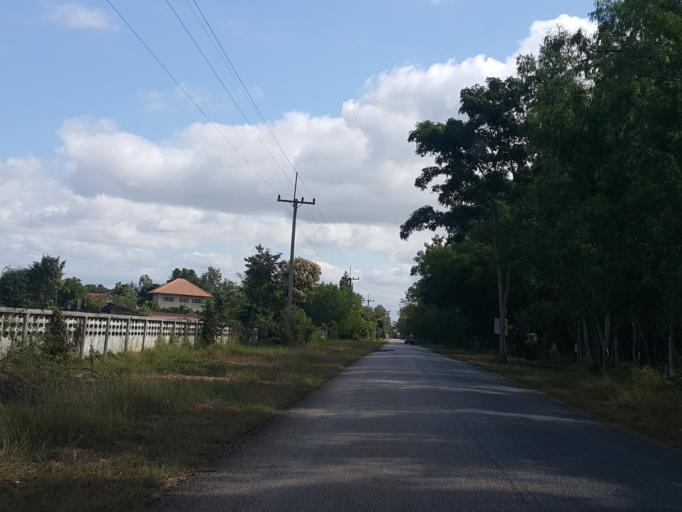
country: TH
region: Lampang
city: Hang Chat
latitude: 18.3480
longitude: 99.3731
